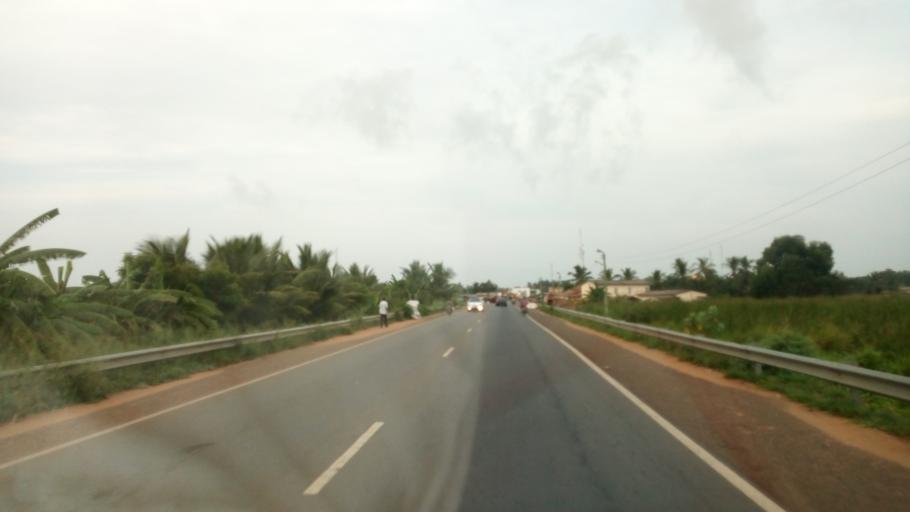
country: GH
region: Volta
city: Keta
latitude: 6.0760
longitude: 1.0409
